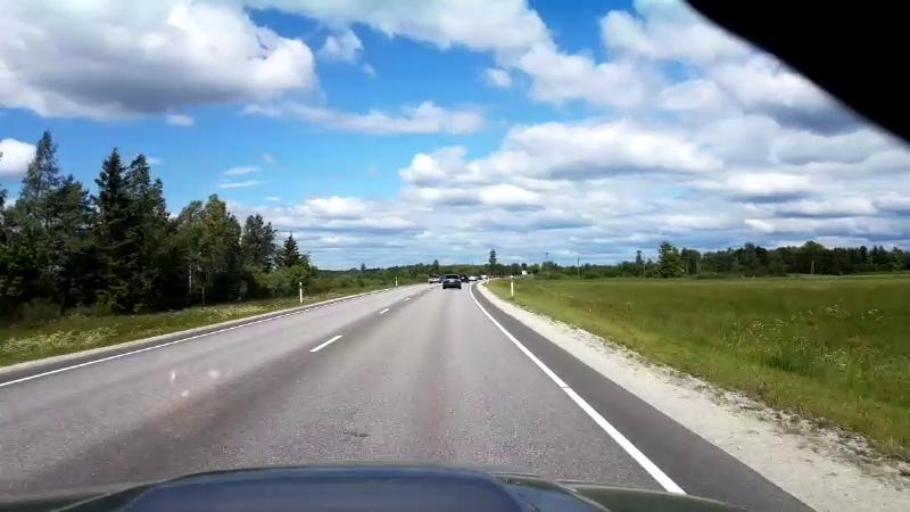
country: EE
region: Paernumaa
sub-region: Sauga vald
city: Sauga
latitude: 58.4903
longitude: 24.5298
